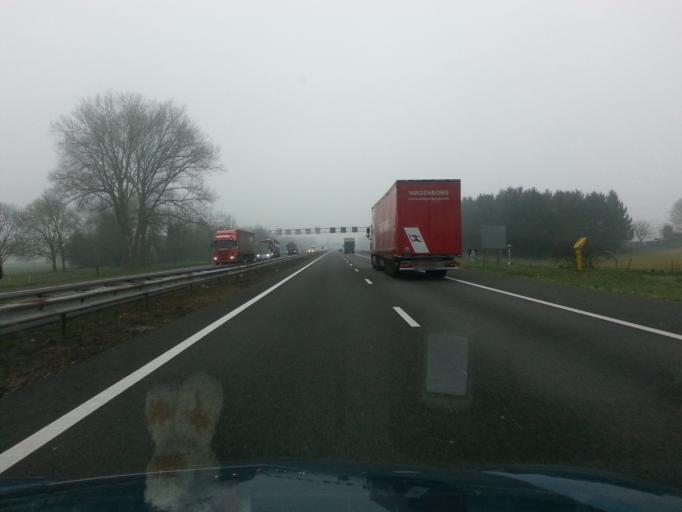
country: NL
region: Gelderland
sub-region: Gemeente Zevenaar
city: Zevenaar
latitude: 51.9122
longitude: 6.1445
